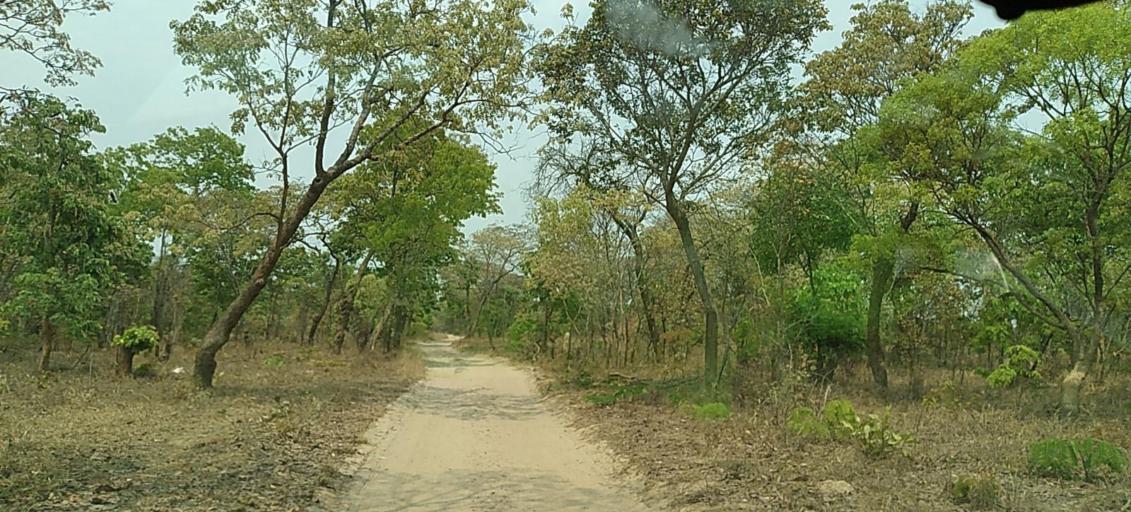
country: ZM
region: North-Western
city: Kabompo
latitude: -13.5542
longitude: 24.4481
